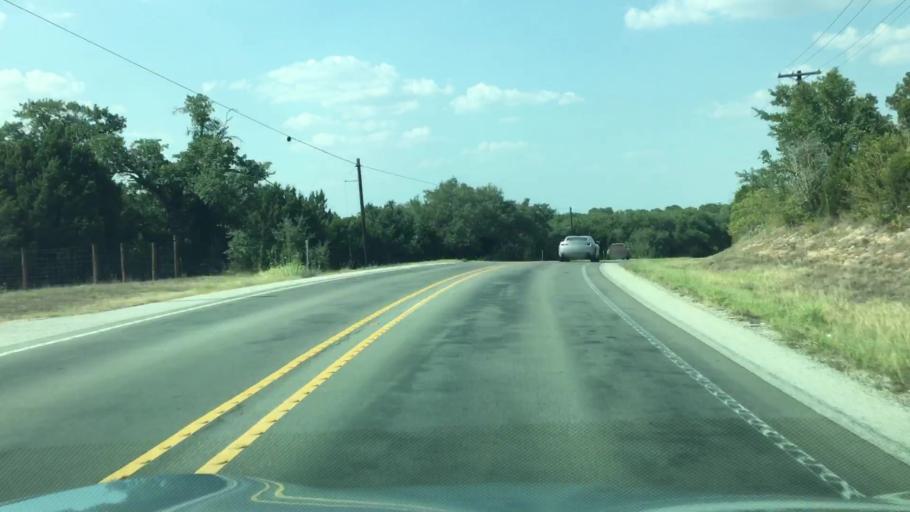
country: US
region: Texas
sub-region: Hays County
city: Woodcreek
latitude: 30.0863
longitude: -98.1006
